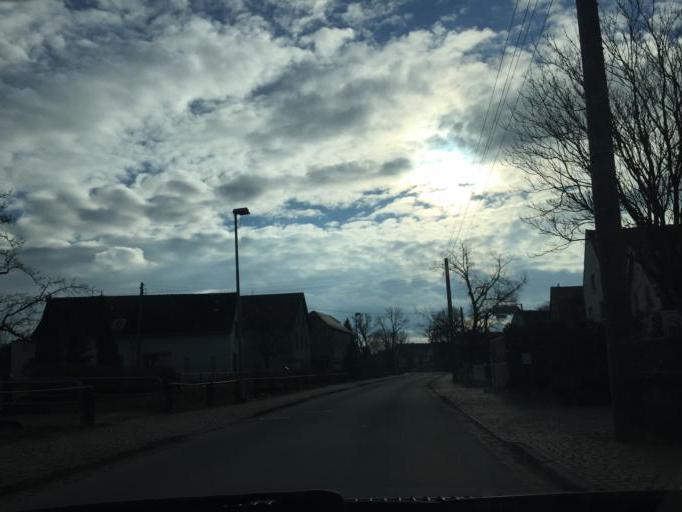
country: DE
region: Saxony
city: Ebersbach
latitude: 51.2459
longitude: 13.6603
